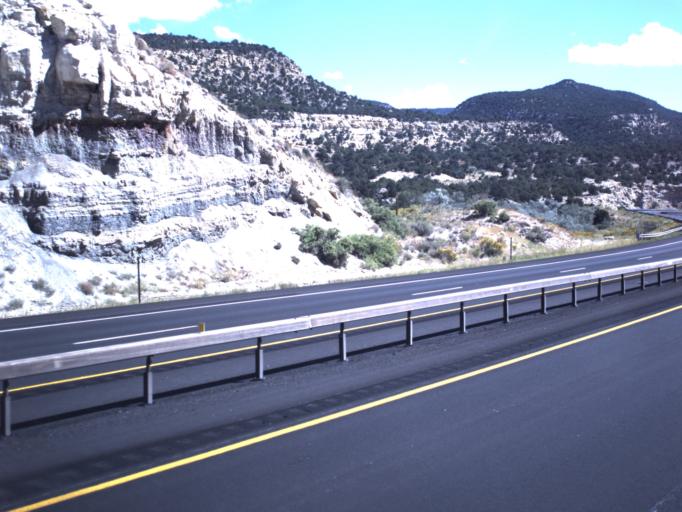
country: US
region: Utah
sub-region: Sevier County
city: Salina
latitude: 38.9098
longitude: -111.7091
